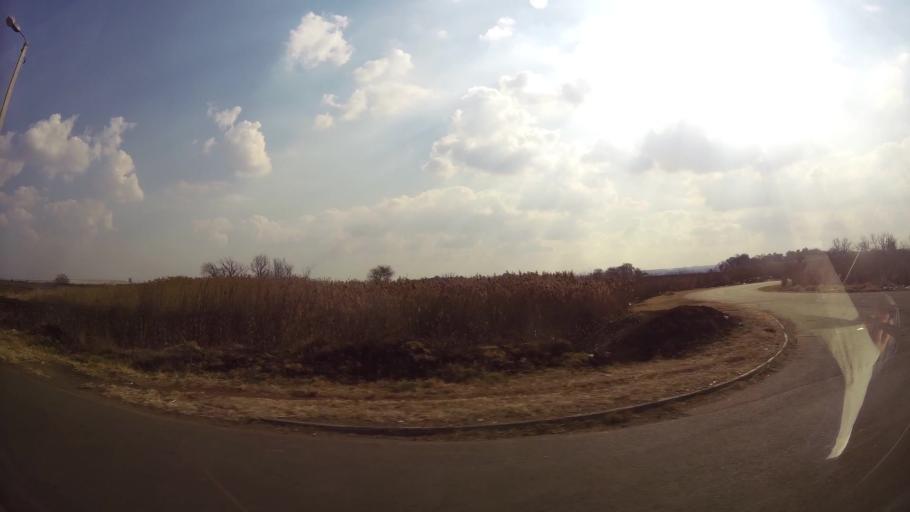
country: ZA
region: Gauteng
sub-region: Ekurhuleni Metropolitan Municipality
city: Germiston
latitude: -26.2998
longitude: 28.2132
